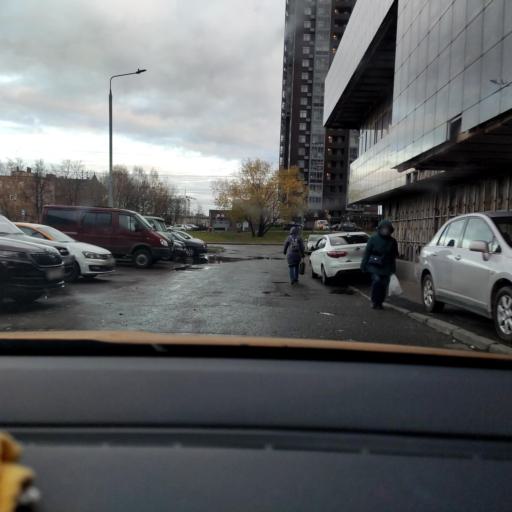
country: RU
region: Moscow
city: Bibirevo
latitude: 55.8809
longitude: 37.5964
